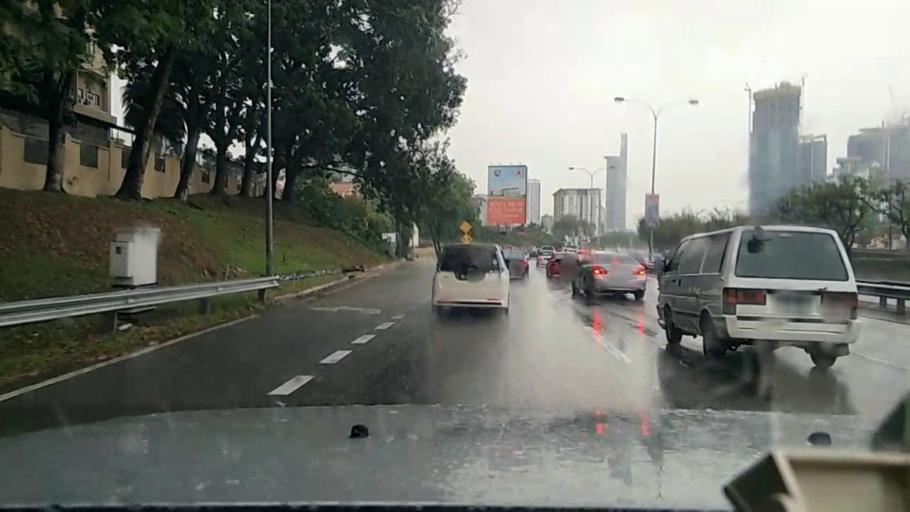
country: MY
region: Kuala Lumpur
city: Kuala Lumpur
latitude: 3.1122
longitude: 101.6850
